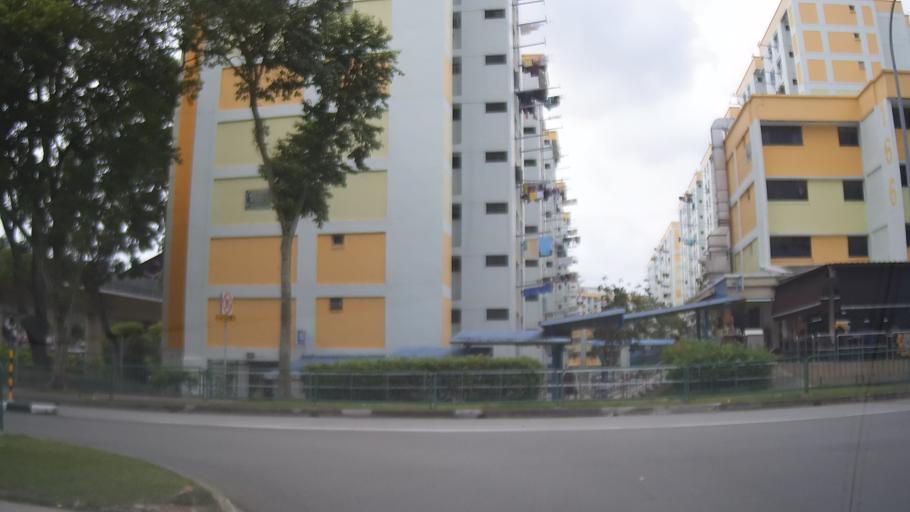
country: MY
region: Johor
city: Johor Bahru
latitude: 1.4332
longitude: 103.7758
